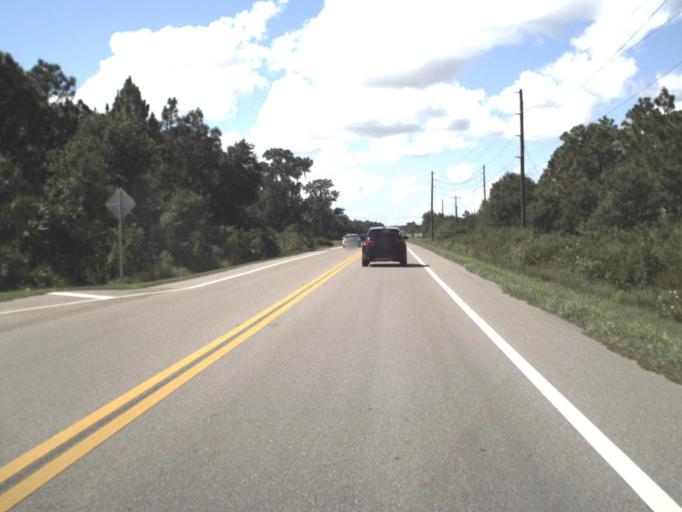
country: US
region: Florida
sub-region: Sarasota County
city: Fruitville
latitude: 27.3956
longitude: -82.2970
